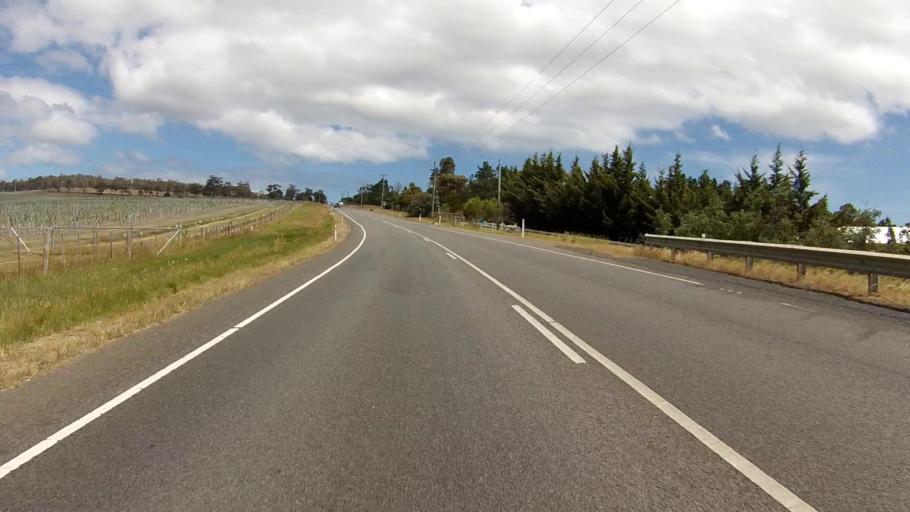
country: AU
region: Tasmania
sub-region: Sorell
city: Sorell
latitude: -42.8120
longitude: 147.6260
